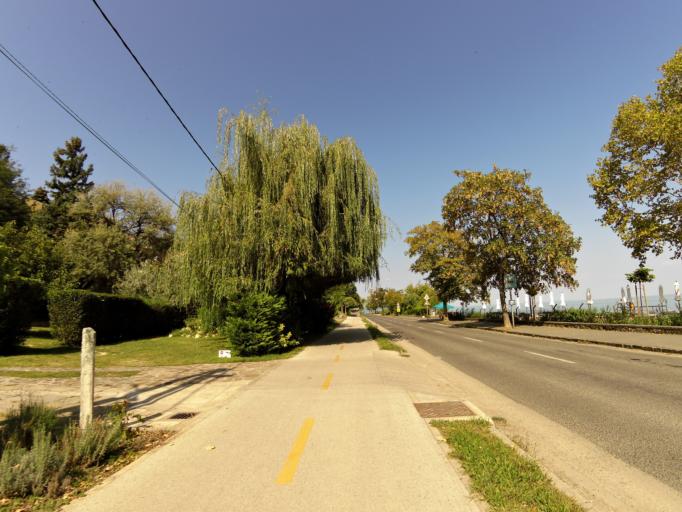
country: HU
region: Veszprem
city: Tihany
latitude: 46.9000
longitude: 17.8974
